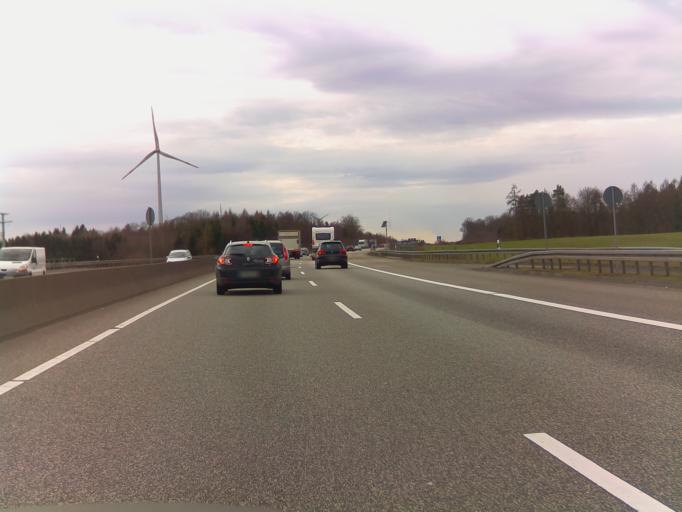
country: DE
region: Hesse
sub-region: Regierungsbezirk Giessen
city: Homberg
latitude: 50.6575
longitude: 9.0164
